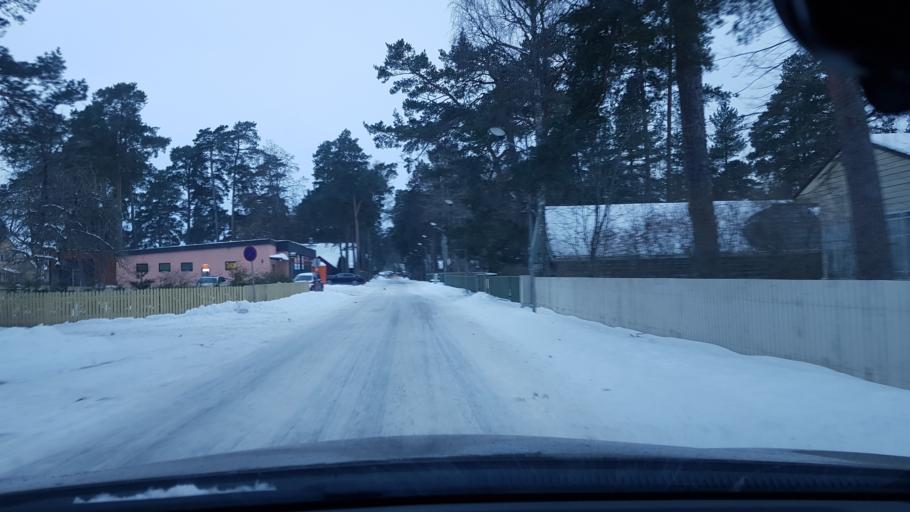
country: EE
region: Harju
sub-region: Loksa linn
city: Loksa
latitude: 59.5764
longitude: 25.9609
